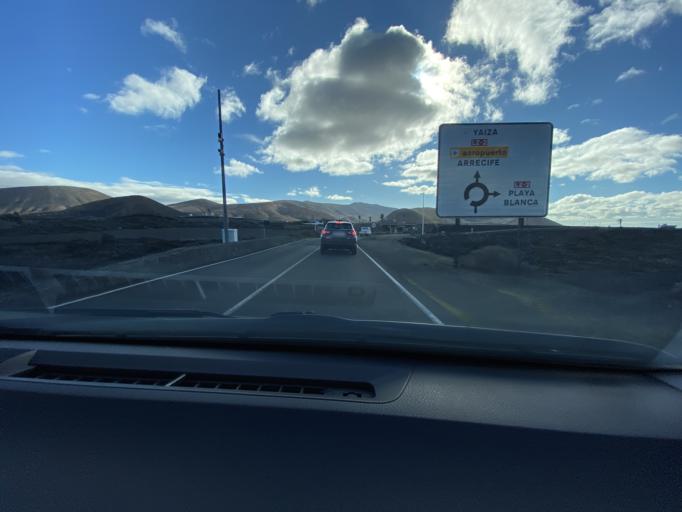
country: ES
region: Canary Islands
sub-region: Provincia de Las Palmas
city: Yaiza
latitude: 28.9595
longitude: -13.7572
